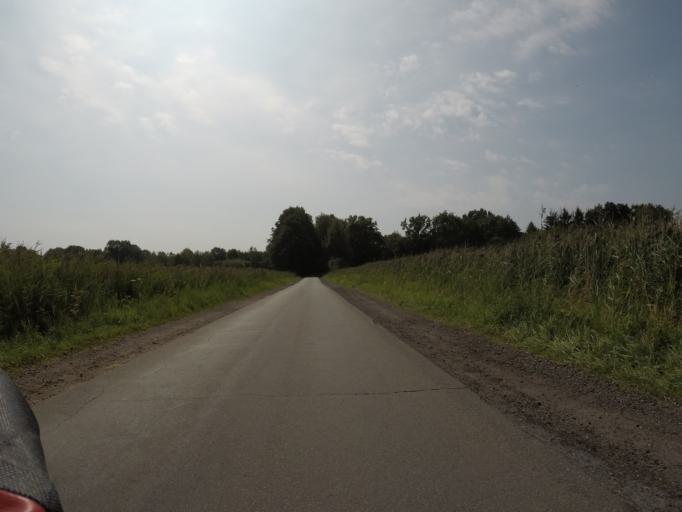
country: DE
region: Schleswig-Holstein
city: Henstedt-Ulzburg
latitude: 53.7689
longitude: 10.0188
